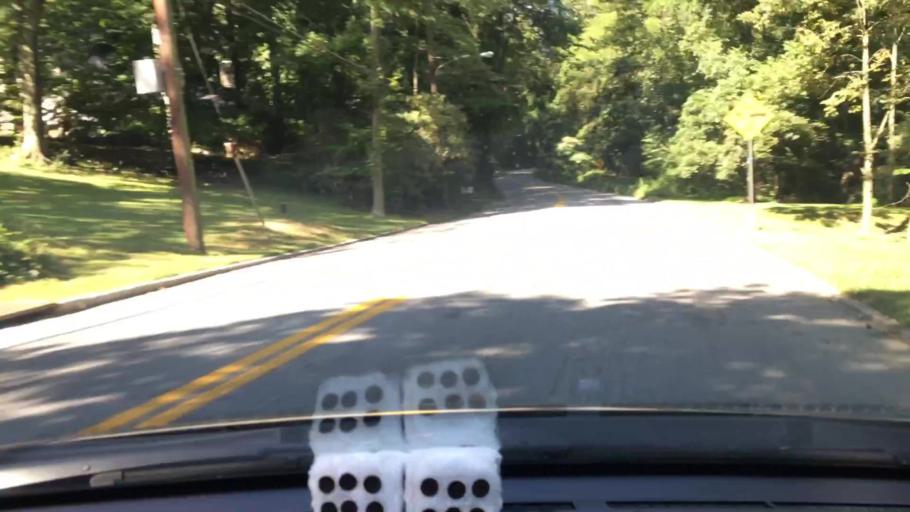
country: US
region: Pennsylvania
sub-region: Montgomery County
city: Bala-Cynwyd
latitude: 40.0174
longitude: -75.2456
